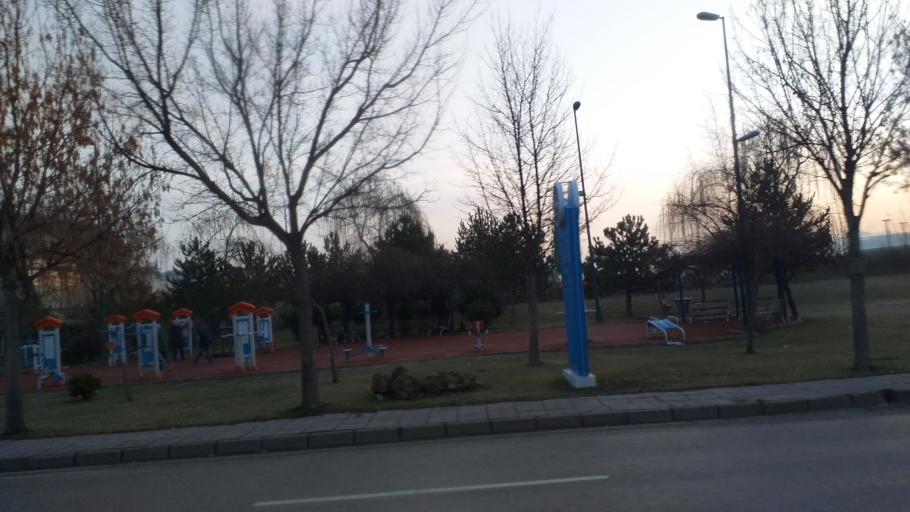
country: TR
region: Ankara
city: Ankara
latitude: 39.9681
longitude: 32.8191
